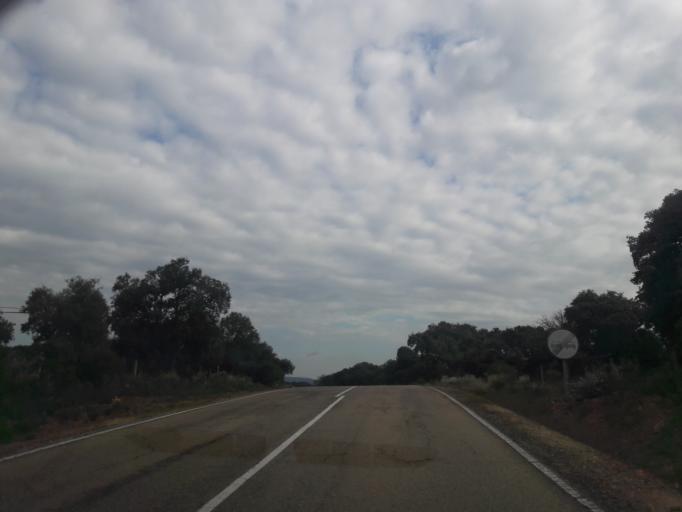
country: ES
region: Castille and Leon
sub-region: Provincia de Salamanca
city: Ciudad Rodrigo
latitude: 40.5606
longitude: -6.5282
